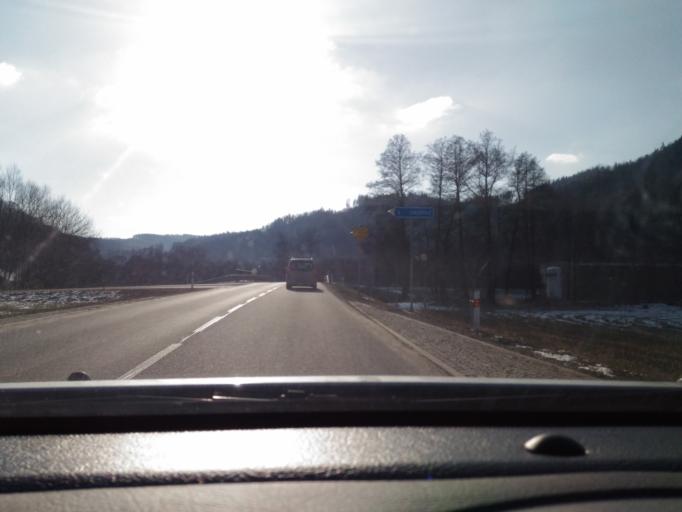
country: CZ
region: South Moravian
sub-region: Okres Brno-Venkov
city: Nedvedice
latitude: 49.4663
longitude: 16.3389
